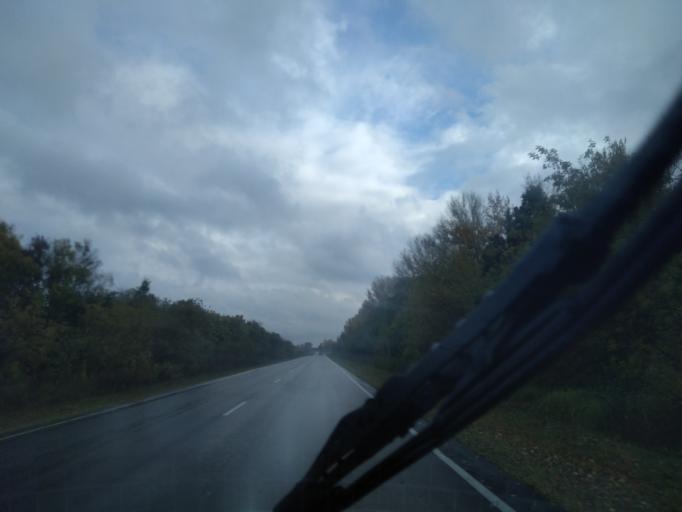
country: RU
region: Tula
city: Teploye
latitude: 53.4578
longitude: 37.7146
